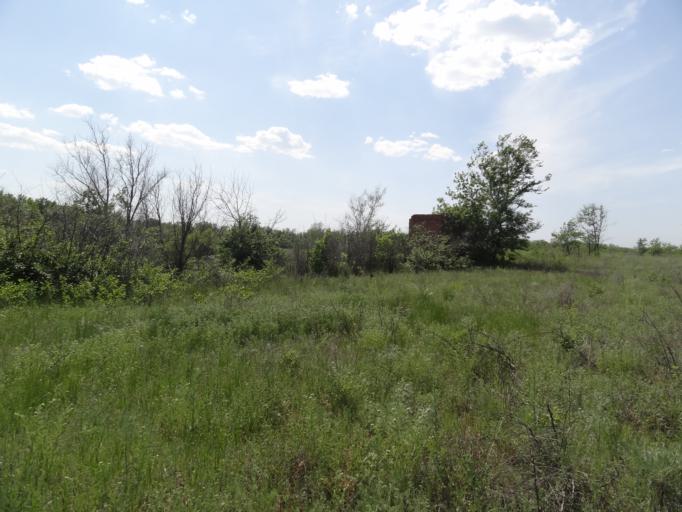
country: RU
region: Saratov
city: Privolzhskiy
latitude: 51.3476
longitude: 46.1496
